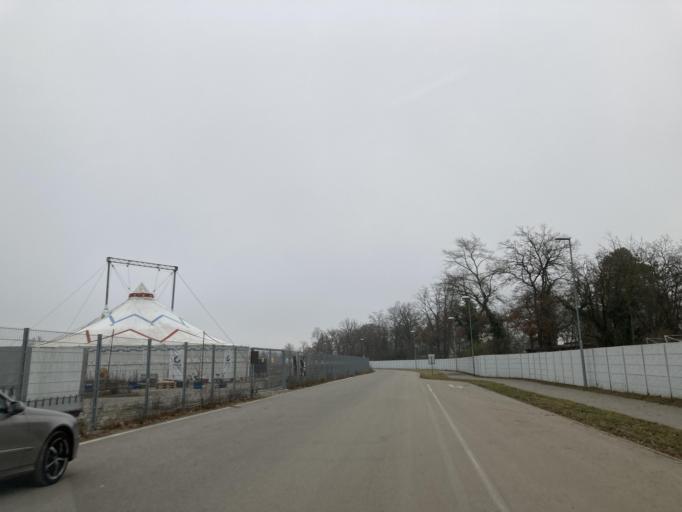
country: DE
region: Baden-Wuerttemberg
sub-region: Freiburg Region
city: Neuenburg am Rhein
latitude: 47.7971
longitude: 7.5505
